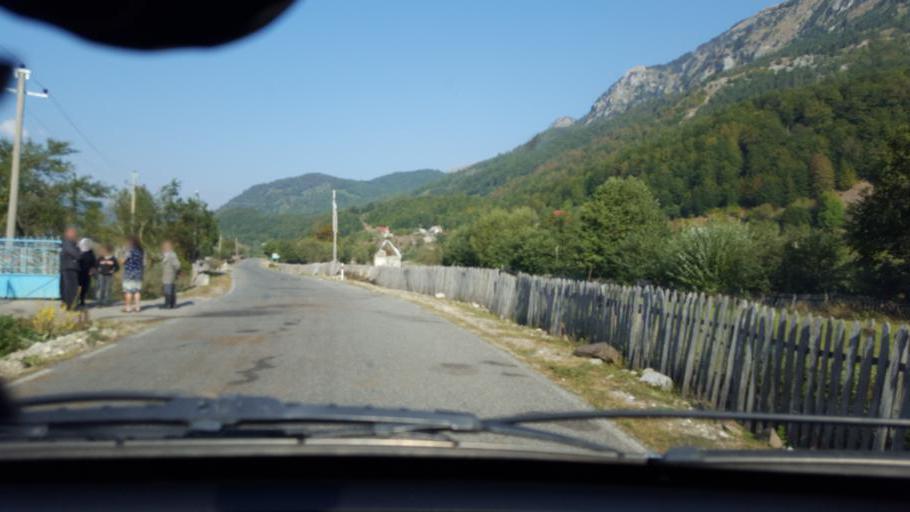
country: ME
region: Andrijevica
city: Andrijevica
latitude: 42.5855
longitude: 19.7237
